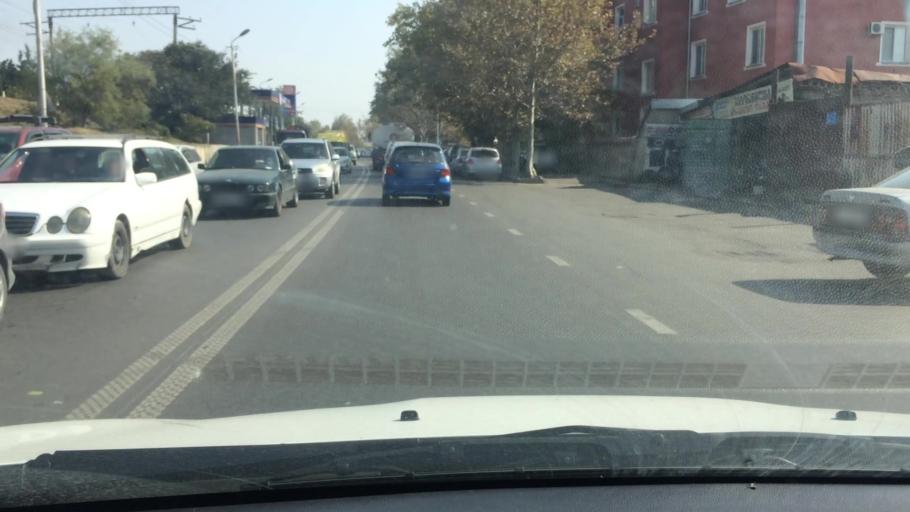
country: GE
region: T'bilisi
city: Tbilisi
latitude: 41.6927
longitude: 44.8259
